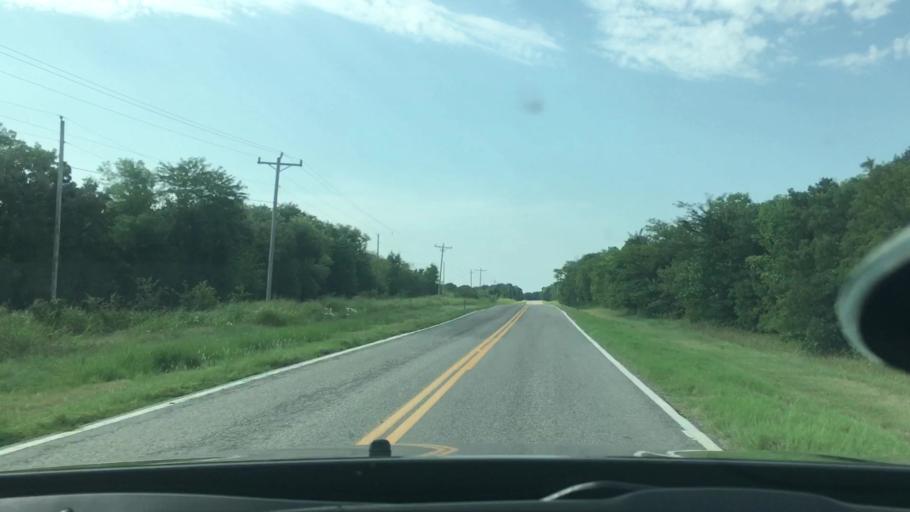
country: US
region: Oklahoma
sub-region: Johnston County
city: Tishomingo
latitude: 34.1794
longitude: -96.5839
